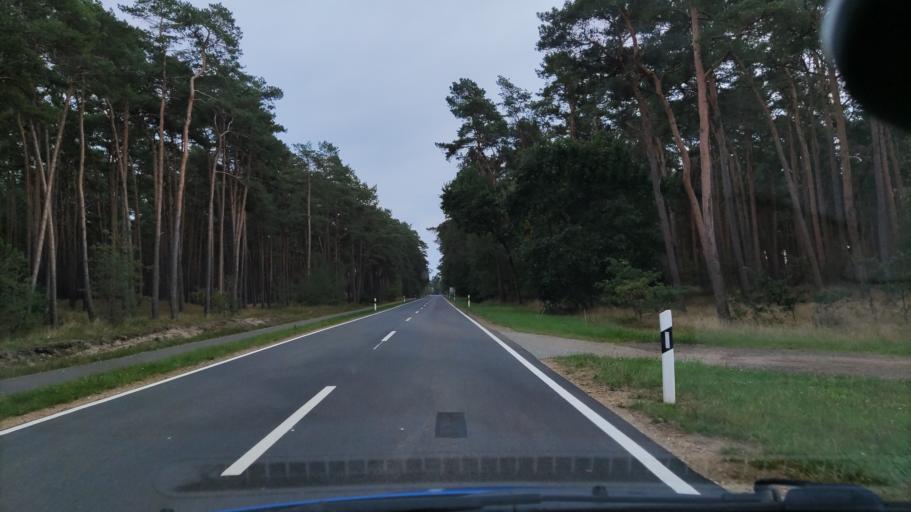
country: DE
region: Lower Saxony
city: Neu Darchau
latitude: 53.2385
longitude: 10.9716
